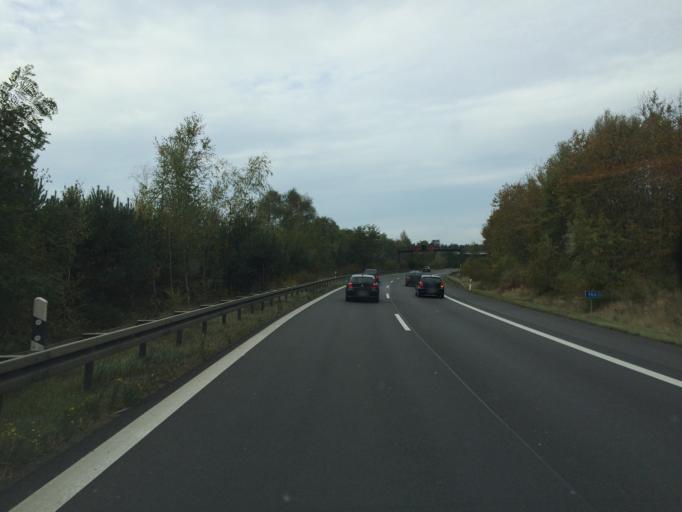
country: DE
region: Brandenburg
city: Fichtenwalde
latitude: 52.2910
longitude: 12.9194
